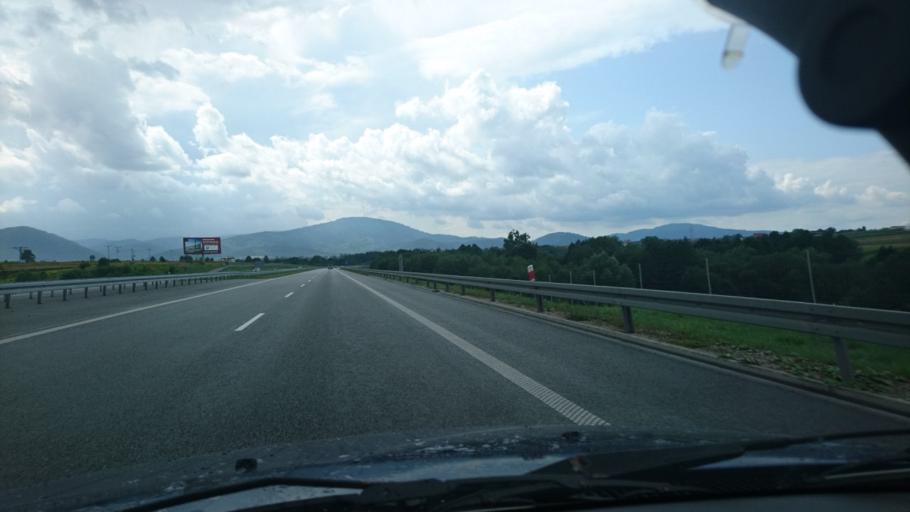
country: PL
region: Silesian Voivodeship
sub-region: Powiat zywiecki
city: Pietrzykowice
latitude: 49.6851
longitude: 19.1553
